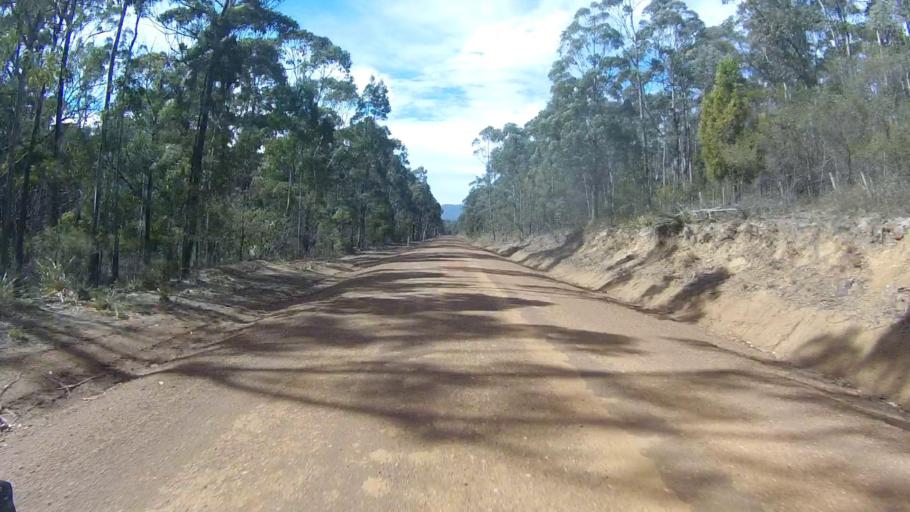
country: AU
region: Tasmania
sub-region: Sorell
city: Sorell
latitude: -42.6163
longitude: 147.9000
